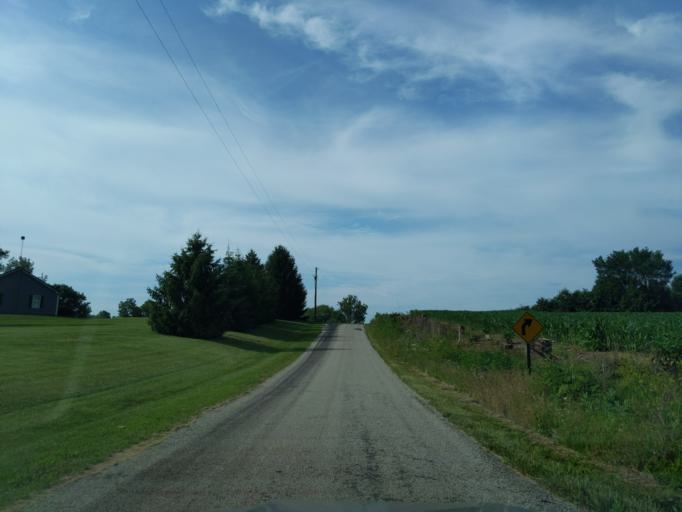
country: US
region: Indiana
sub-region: Ripley County
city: Osgood
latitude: 39.2105
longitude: -85.3893
